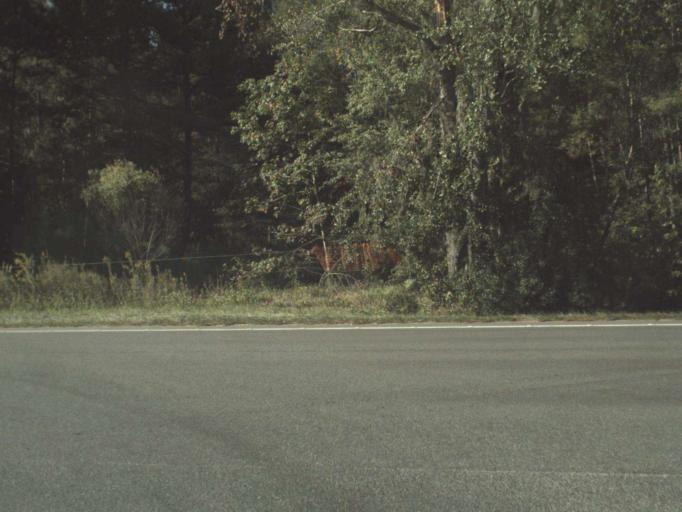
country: US
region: Florida
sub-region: Gadsden County
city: Quincy
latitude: 30.3903
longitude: -84.6279
